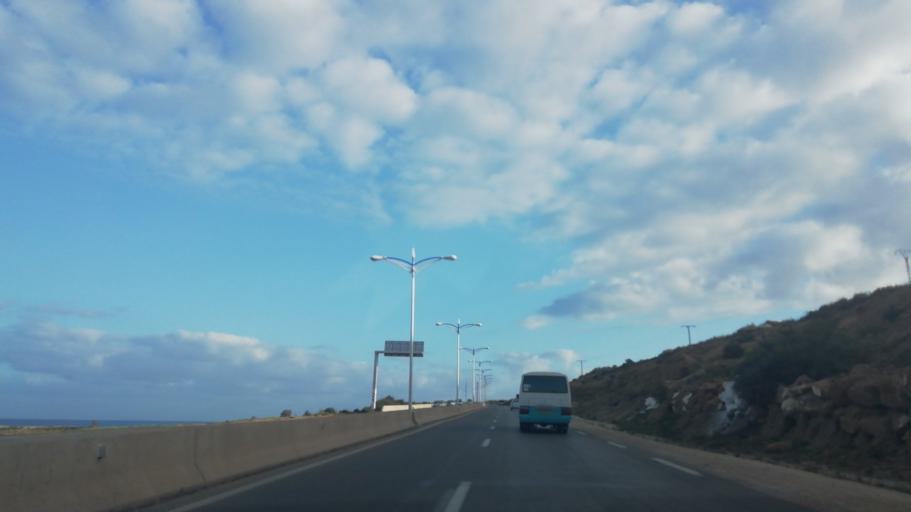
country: DZ
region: Mostaganem
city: Mostaganem
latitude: 36.0391
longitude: 0.1438
